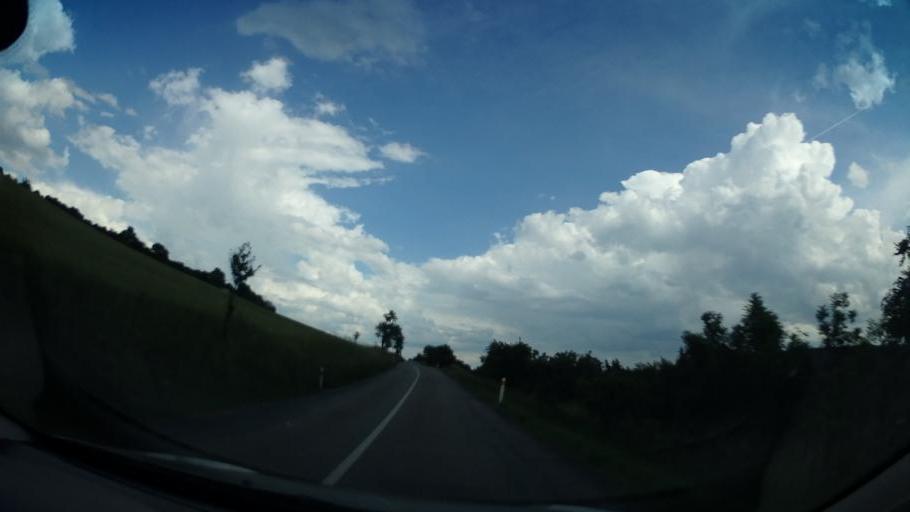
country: CZ
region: South Moravian
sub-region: Okres Brno-Venkov
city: Dolni Loucky
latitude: 49.3753
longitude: 16.3572
